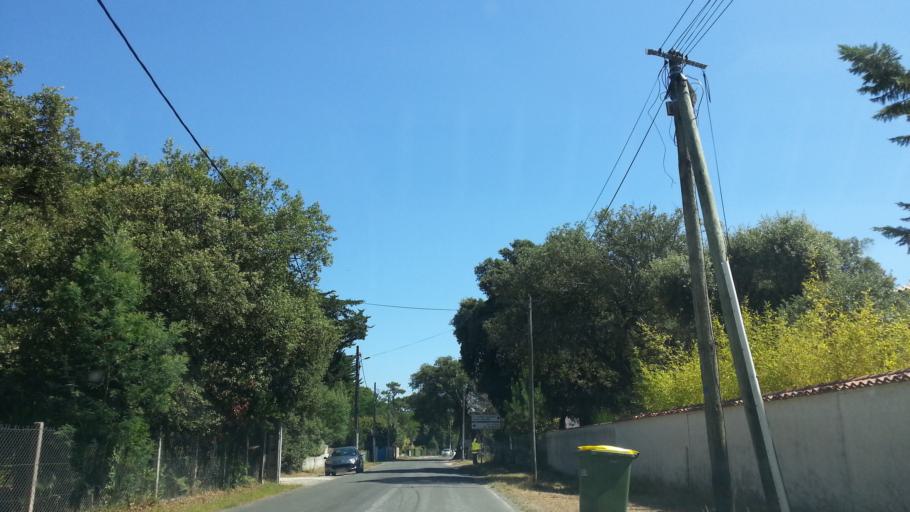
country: FR
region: Poitou-Charentes
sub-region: Departement de la Charente-Maritime
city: Dolus-d'Oleron
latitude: 45.8833
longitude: -1.2567
